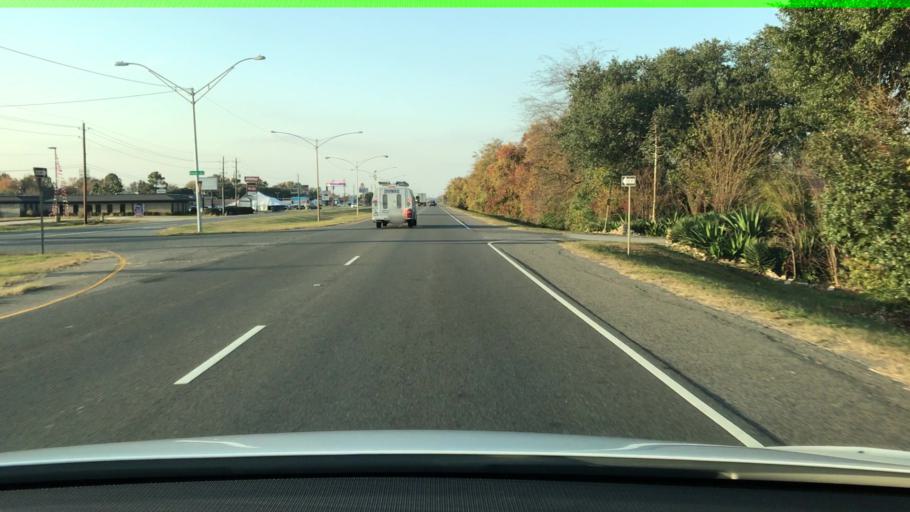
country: US
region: Louisiana
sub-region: Bossier Parish
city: Bossier City
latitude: 32.4206
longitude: -93.7052
